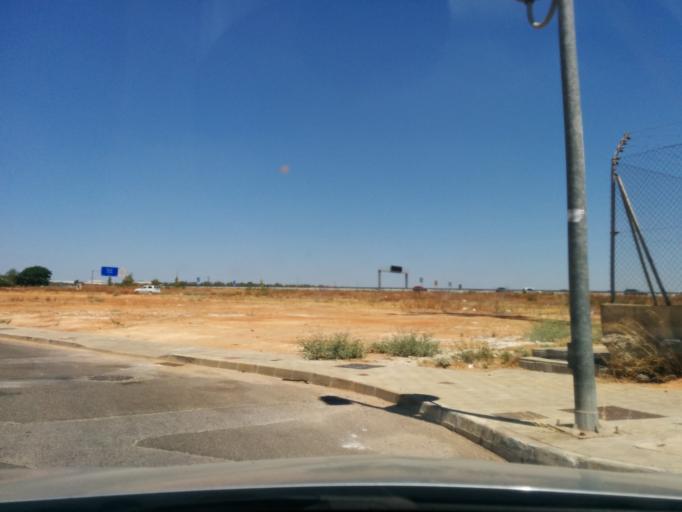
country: ES
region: Andalusia
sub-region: Provincia de Sevilla
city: Benacazon
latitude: 37.3574
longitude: -6.1933
